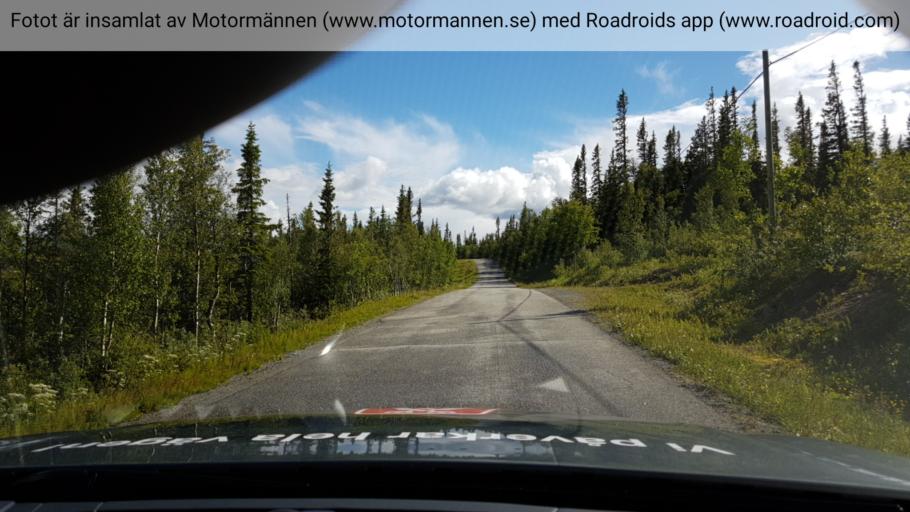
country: SE
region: Jaemtland
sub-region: Bergs Kommun
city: Hoverberg
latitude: 63.0132
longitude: 13.9422
